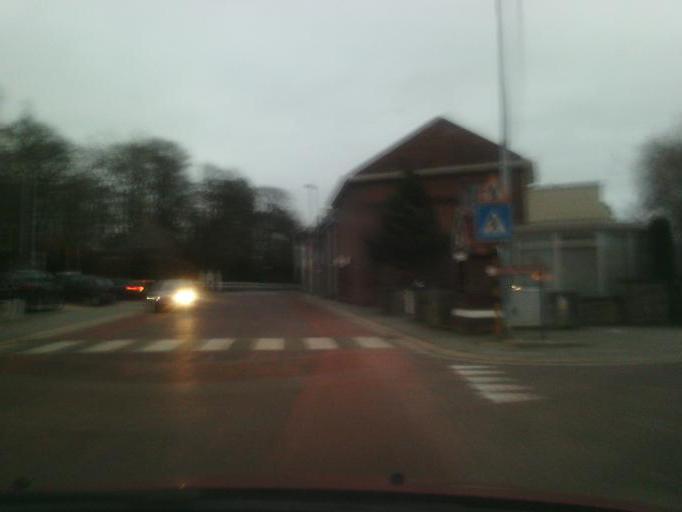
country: BE
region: Flanders
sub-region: Provincie Oost-Vlaanderen
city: Waasmunster
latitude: 51.1117
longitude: 4.0908
